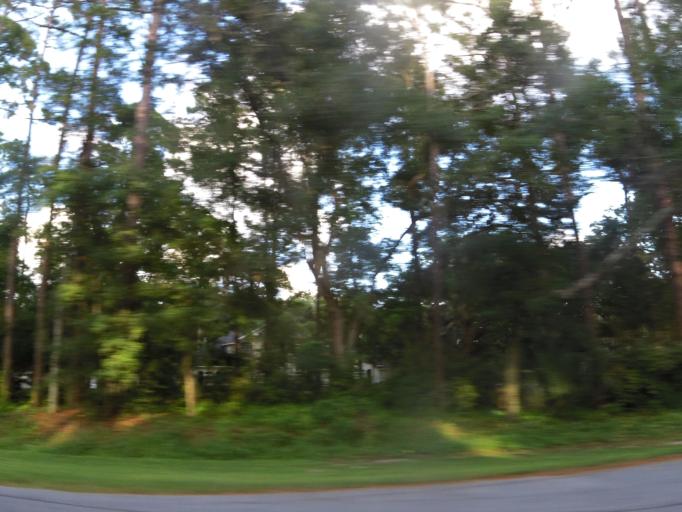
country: US
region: Georgia
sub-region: Glynn County
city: Saint Simon Mills
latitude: 31.1762
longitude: -81.4009
